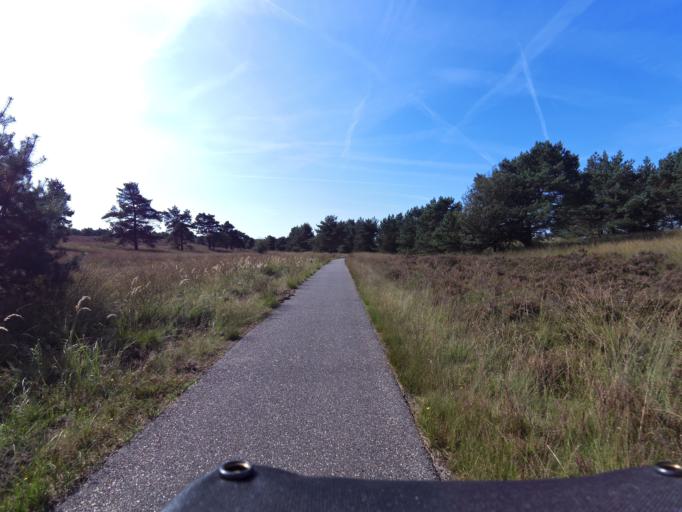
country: NL
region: Gelderland
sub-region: Gemeente Apeldoorn
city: Uddel
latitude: 52.2075
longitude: 5.8609
